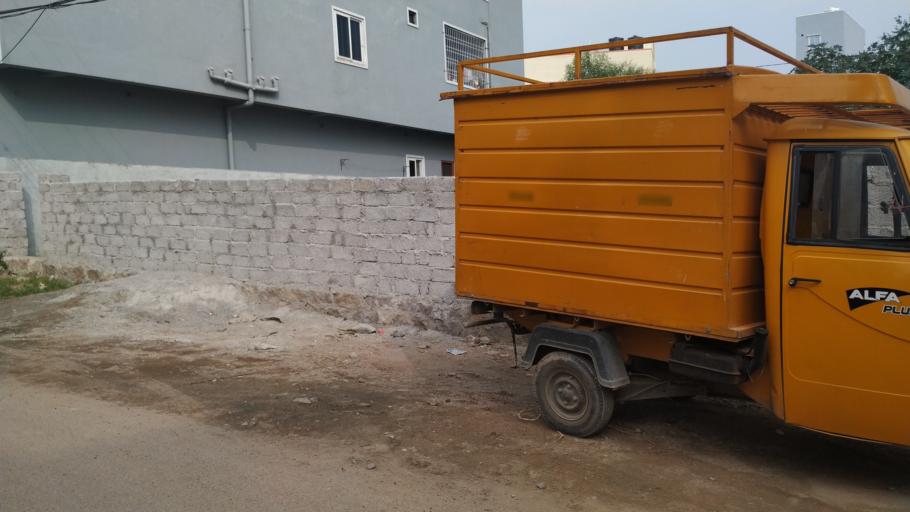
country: IN
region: Telangana
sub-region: Medak
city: Serilingampalle
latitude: 17.4918
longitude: 78.3201
